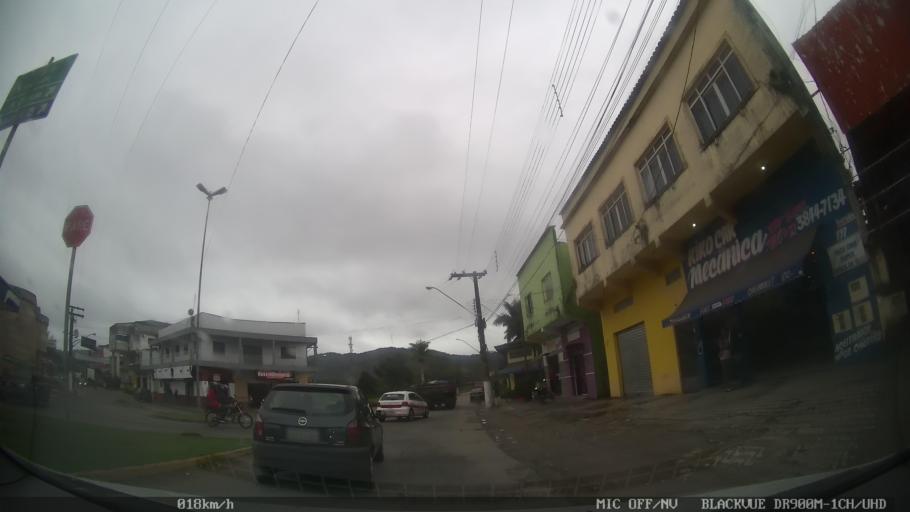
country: BR
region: Sao Paulo
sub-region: Juquia
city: Juquia
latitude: -24.3270
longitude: -47.6317
